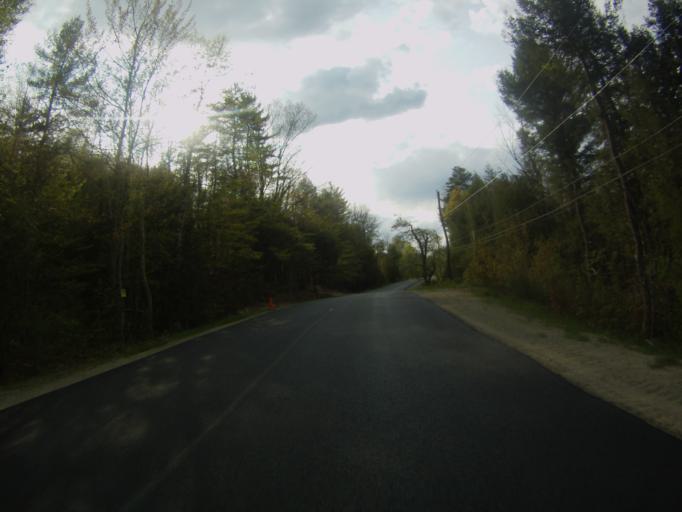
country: US
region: New York
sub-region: Warren County
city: Warrensburg
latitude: 43.8374
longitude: -73.7779
